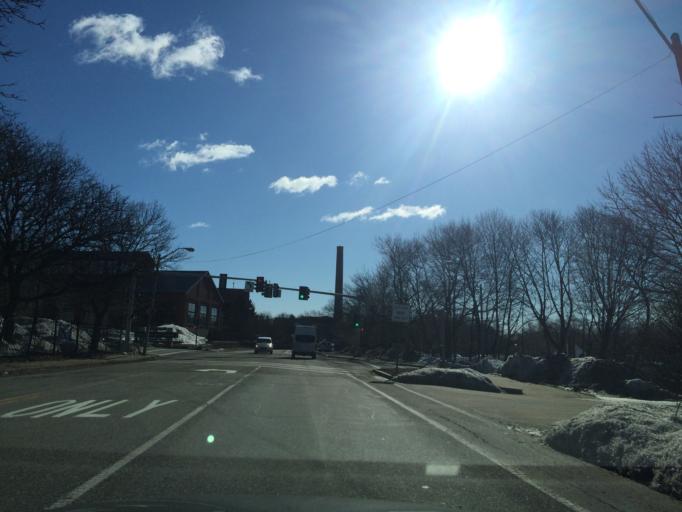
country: US
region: Massachusetts
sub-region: Middlesex County
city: Watertown
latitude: 42.3625
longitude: -71.1689
